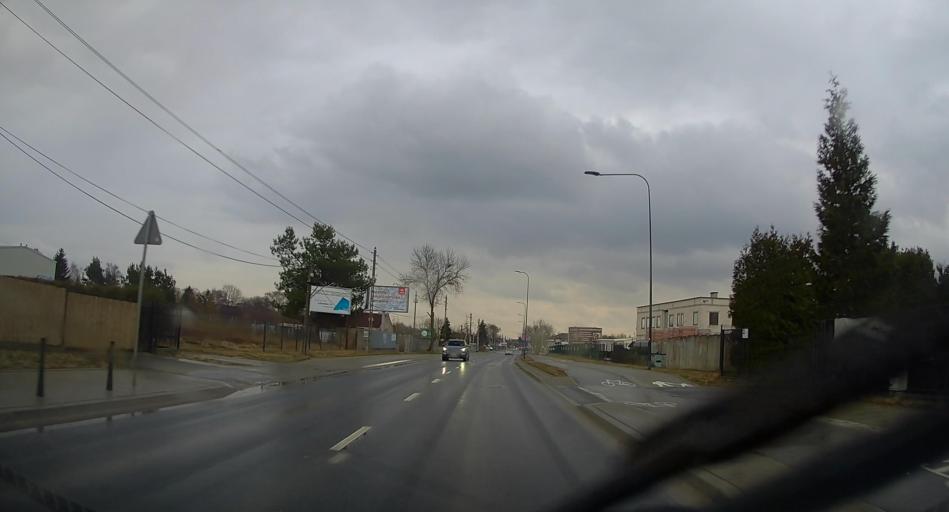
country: PL
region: Masovian Voivodeship
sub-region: Warszawa
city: Wawer
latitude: 52.1956
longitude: 21.1368
